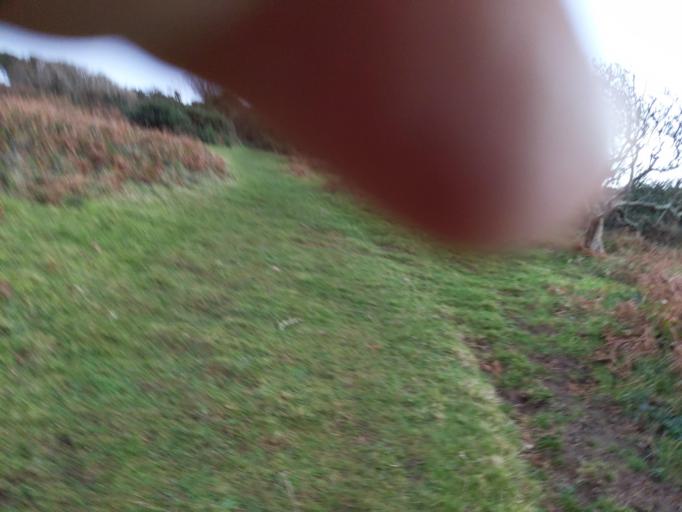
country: GB
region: England
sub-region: Cornwall
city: Fowey
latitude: 50.3258
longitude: -4.6009
